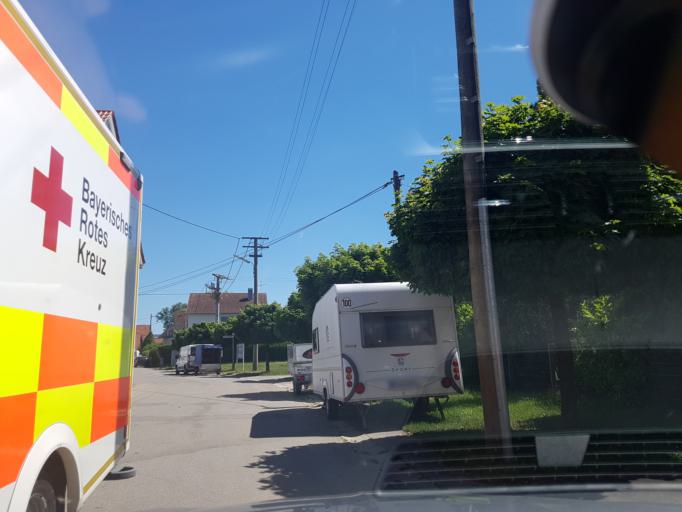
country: DE
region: Bavaria
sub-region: Swabia
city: Weissenhorn
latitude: 48.3153
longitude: 10.1534
